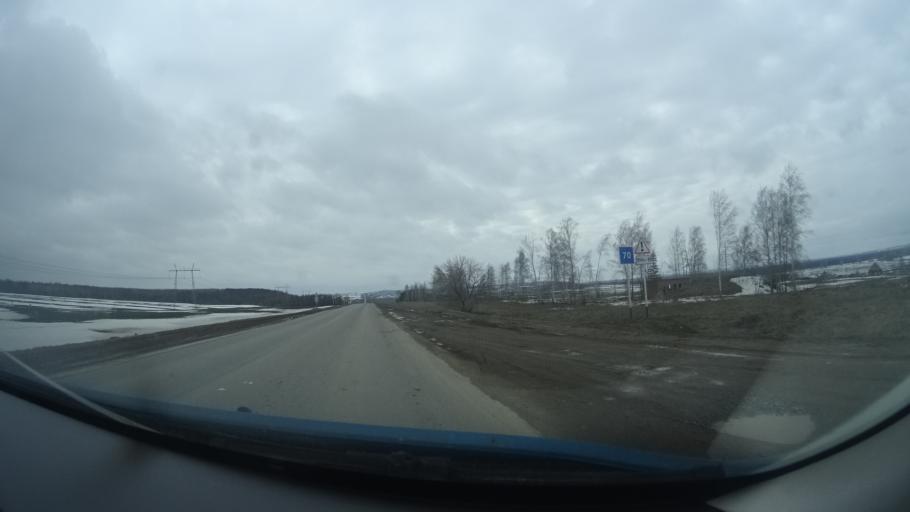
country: RU
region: Bashkortostan
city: Birsk
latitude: 55.4904
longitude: 55.6002
